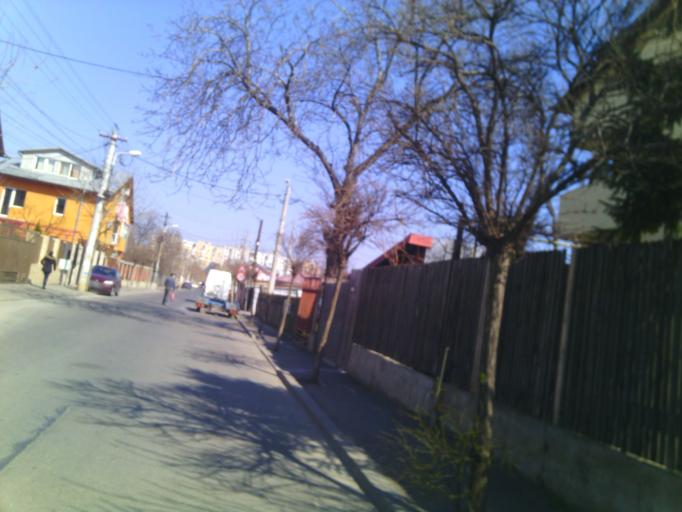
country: RO
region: Ilfov
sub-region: Comuna Jilava
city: Jilava
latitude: 44.3745
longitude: 26.0965
